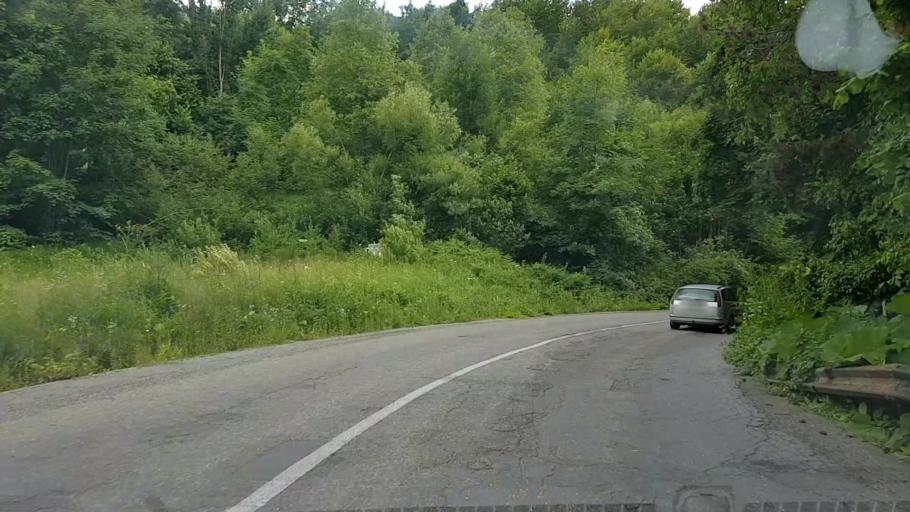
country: RO
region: Neamt
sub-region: Comuna Pangarati
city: Pangarati
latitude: 46.9476
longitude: 26.1312
